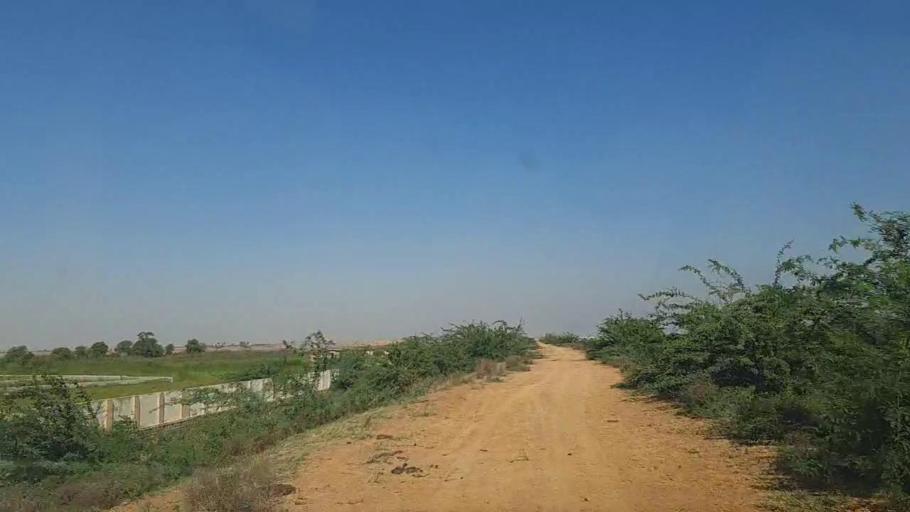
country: PK
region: Sindh
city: Thatta
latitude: 24.8195
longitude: 67.9897
